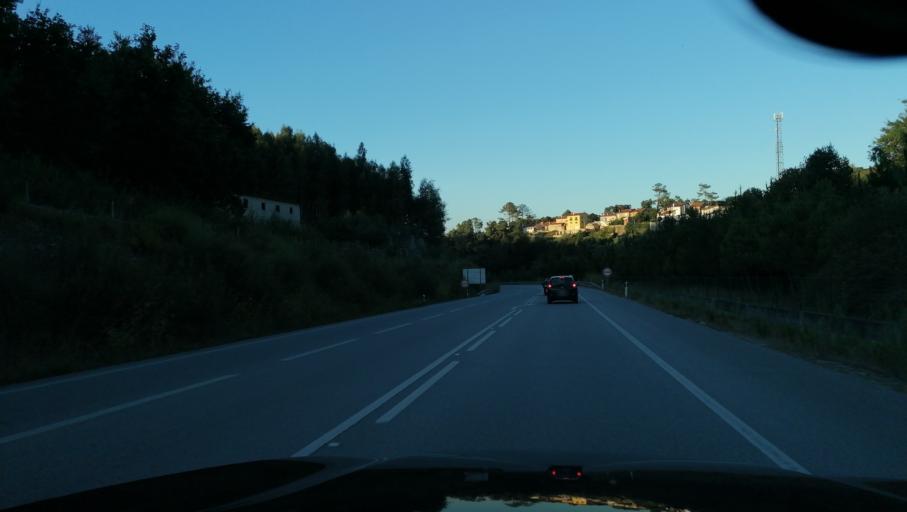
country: PT
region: Aveiro
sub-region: Agueda
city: Agueda
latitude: 40.5613
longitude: -8.4535
